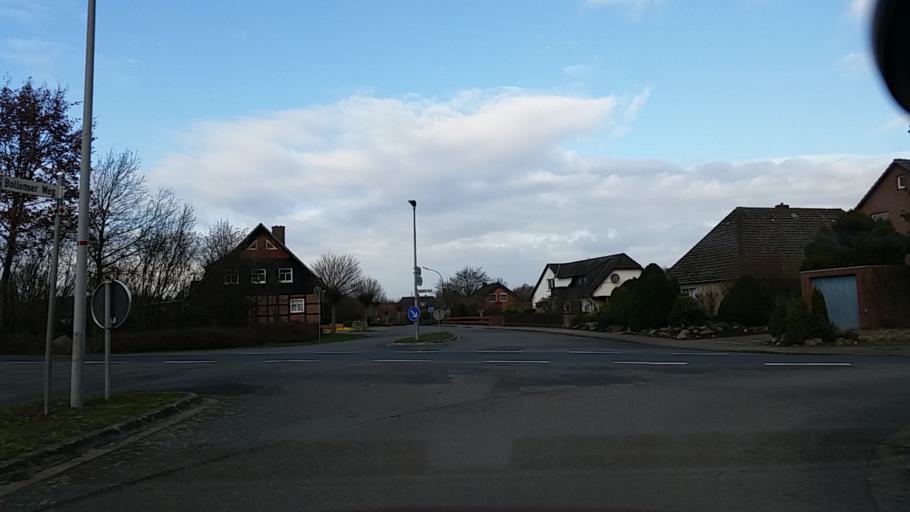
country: DE
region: Lower Saxony
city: Wieren
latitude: 52.8874
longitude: 10.6505
